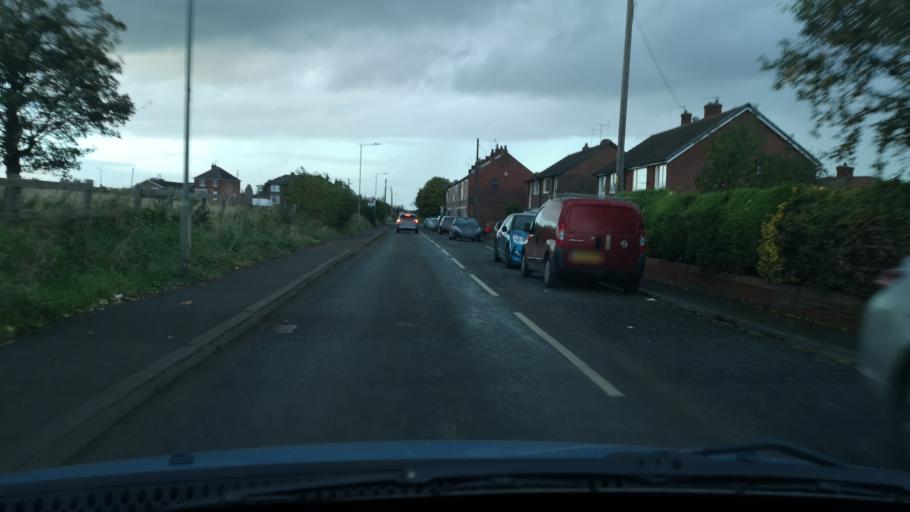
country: GB
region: England
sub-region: Doncaster
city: Norton
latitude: 53.6304
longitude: -1.1847
